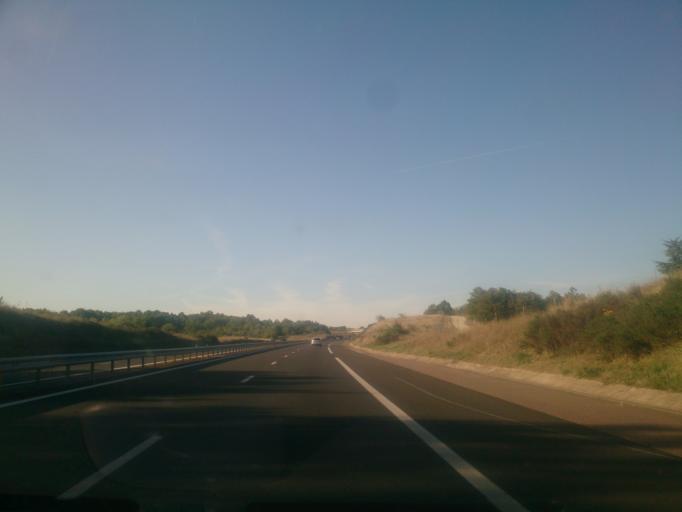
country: FR
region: Midi-Pyrenees
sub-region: Departement du Lot
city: Pradines
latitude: 44.5679
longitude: 1.5124
